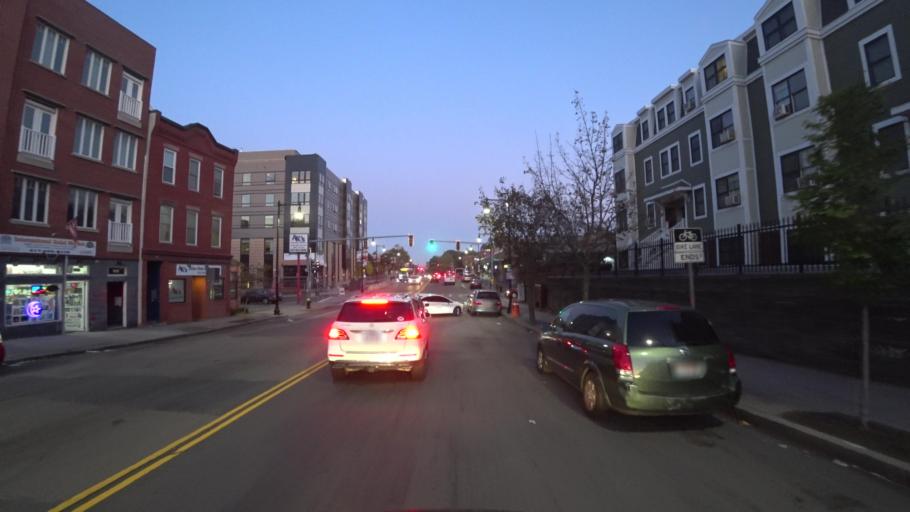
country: US
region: Massachusetts
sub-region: Norfolk County
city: Brookline
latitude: 42.3317
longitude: -71.0966
